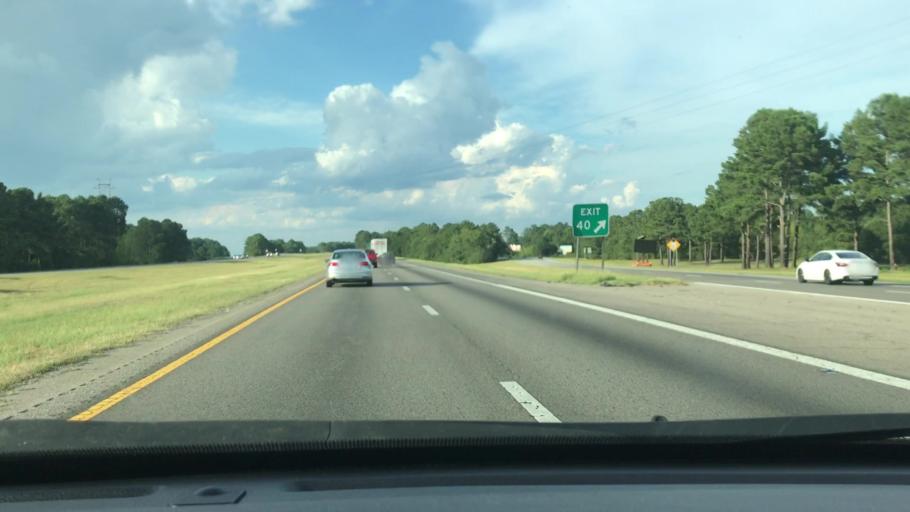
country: US
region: North Carolina
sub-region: Cumberland County
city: Hope Mills
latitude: 34.9244
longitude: -78.9436
